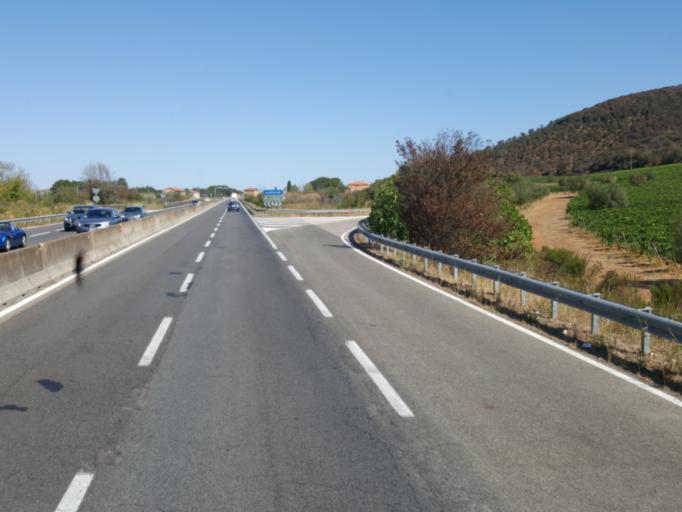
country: IT
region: Tuscany
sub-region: Provincia di Grosseto
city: Fonteblanda
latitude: 42.6325
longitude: 11.1372
